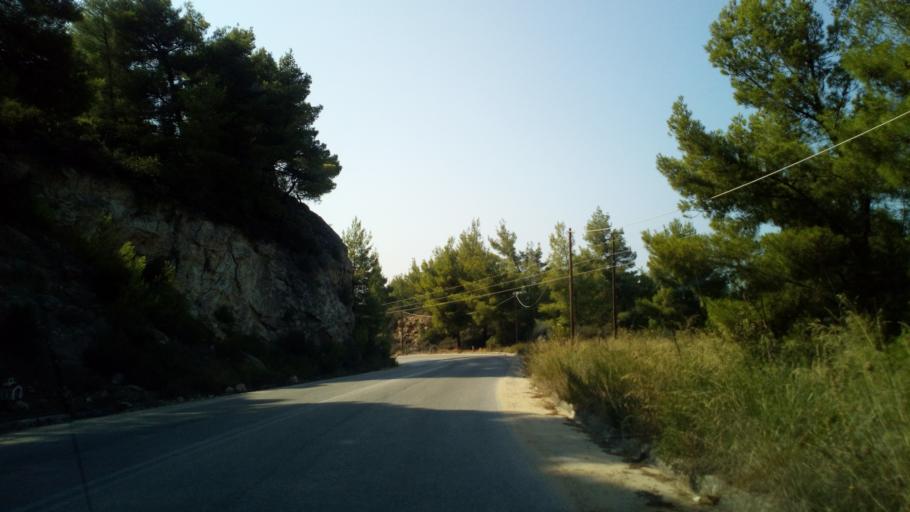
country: GR
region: Central Macedonia
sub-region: Nomos Chalkidikis
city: Sarti
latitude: 40.1132
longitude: 23.9835
